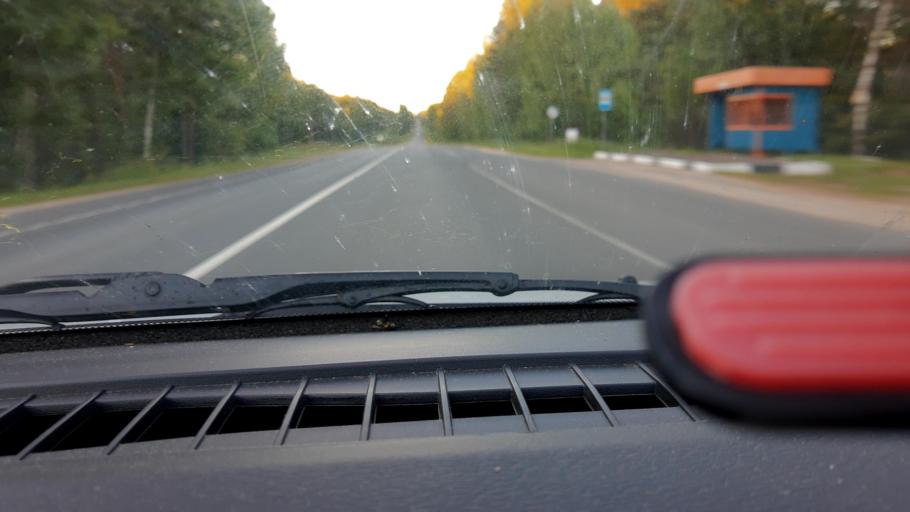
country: RU
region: Nizjnij Novgorod
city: Uren'
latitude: 57.2958
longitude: 45.6565
